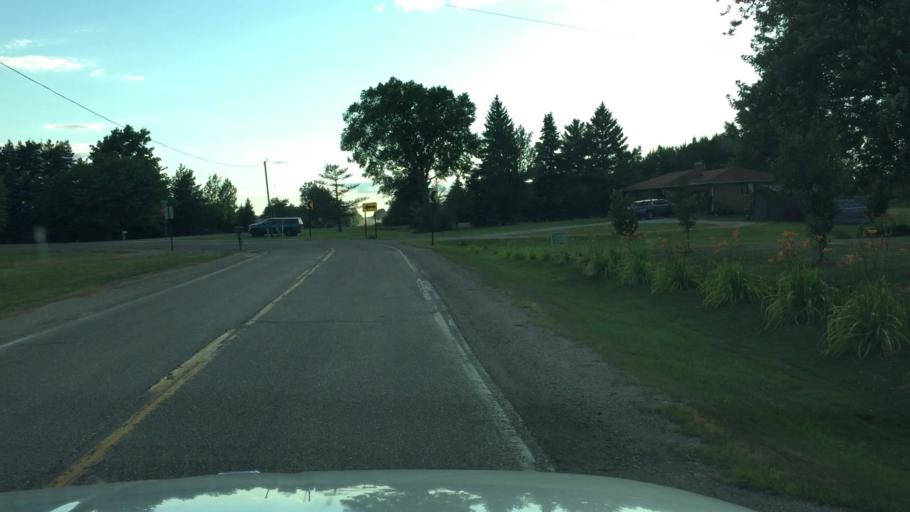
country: US
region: Michigan
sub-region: Saint Clair County
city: Capac
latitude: 43.0271
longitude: -82.9367
